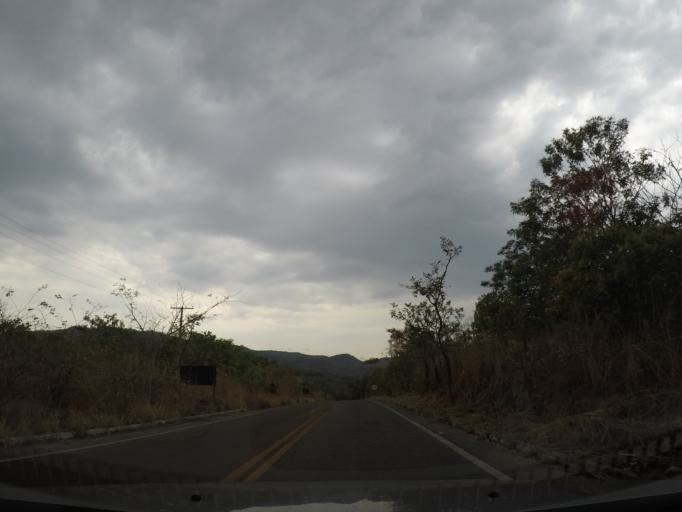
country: BR
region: Goias
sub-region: Pirenopolis
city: Pirenopolis
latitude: -15.8472
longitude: -48.9243
